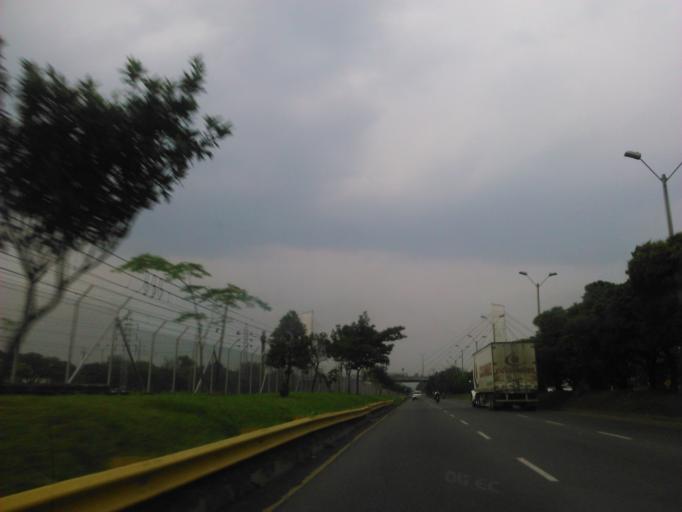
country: CO
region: Antioquia
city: Itagui
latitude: 6.2006
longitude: -75.5796
